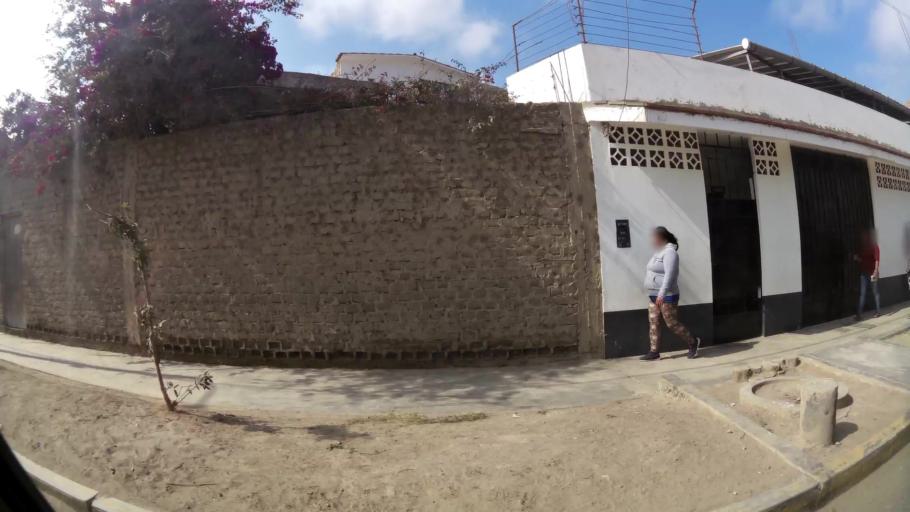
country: PE
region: La Libertad
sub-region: Provincia de Trujillo
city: Trujillo
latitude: -8.1176
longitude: -79.0152
